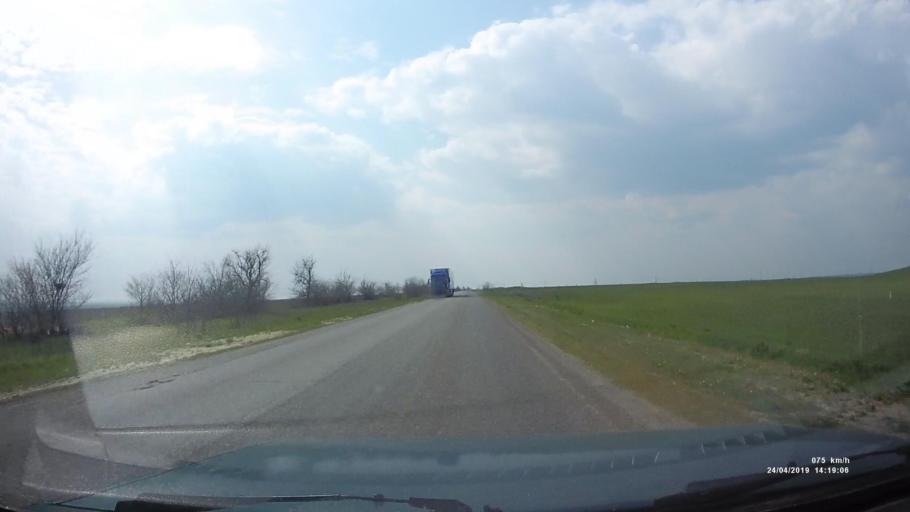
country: RU
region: Kalmykiya
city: Arshan'
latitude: 46.3044
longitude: 44.1816
